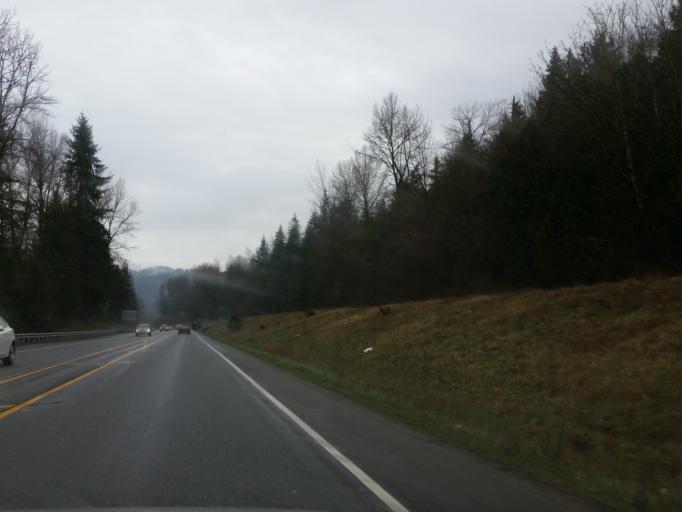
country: US
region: Washington
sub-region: Snohomish County
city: Cathcart
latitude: 47.8222
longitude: -122.0617
